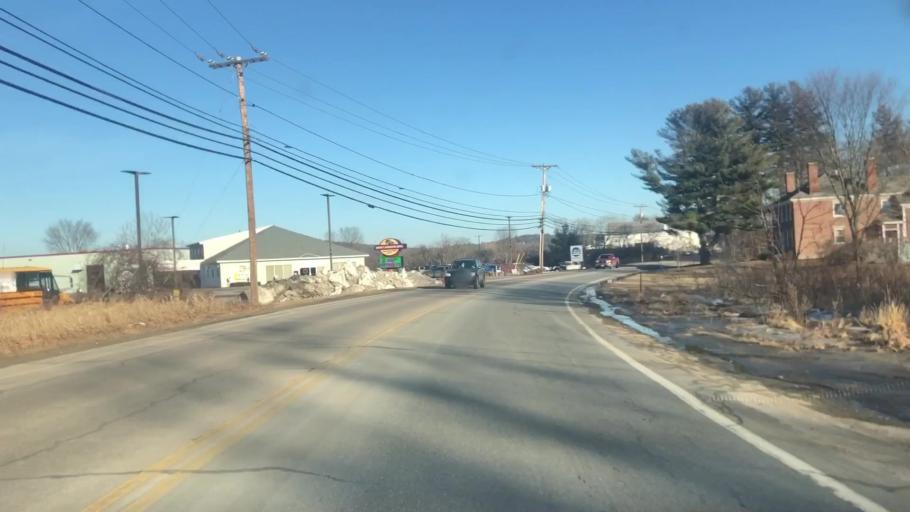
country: US
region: New Hampshire
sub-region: Hillsborough County
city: Milford
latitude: 42.8412
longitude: -71.6849
